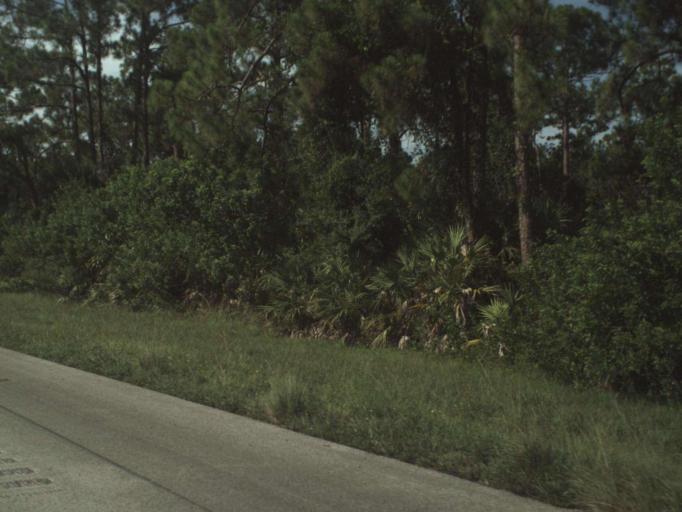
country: US
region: Florida
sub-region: Indian River County
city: Roseland
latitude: 27.8163
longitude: -80.5507
